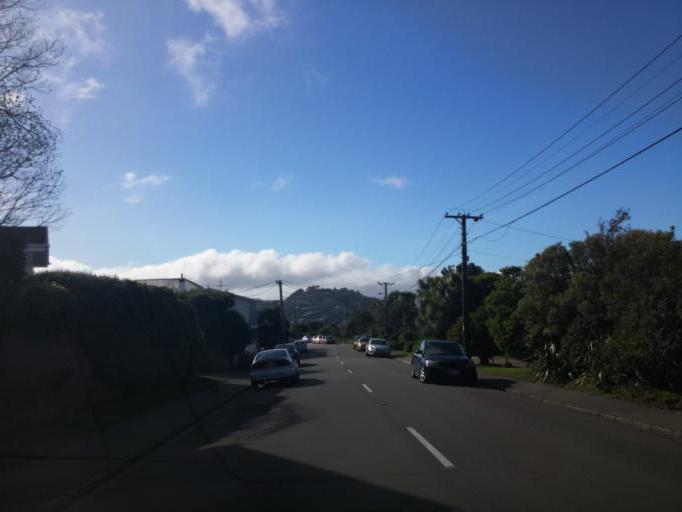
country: NZ
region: Wellington
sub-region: Wellington City
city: Kelburn
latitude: -41.2898
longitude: 174.7498
